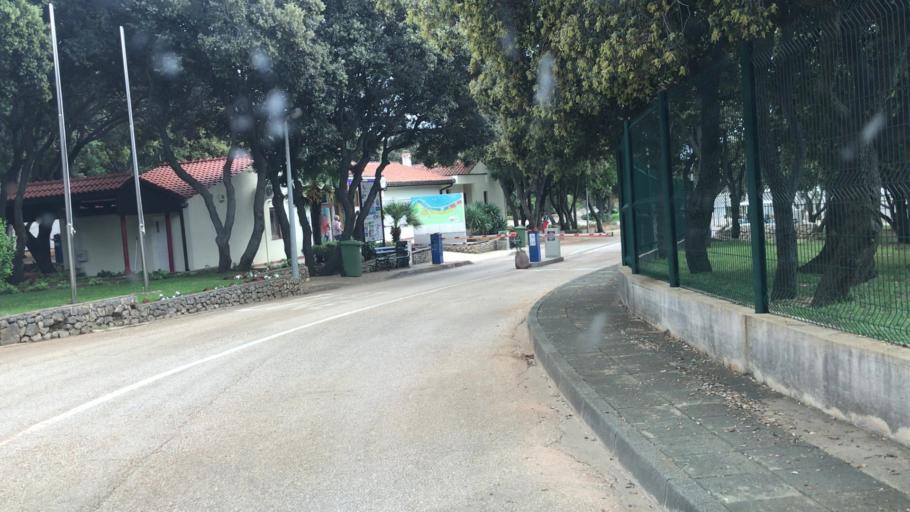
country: HR
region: Licko-Senjska
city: Novalja
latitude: 44.5389
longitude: 14.8861
